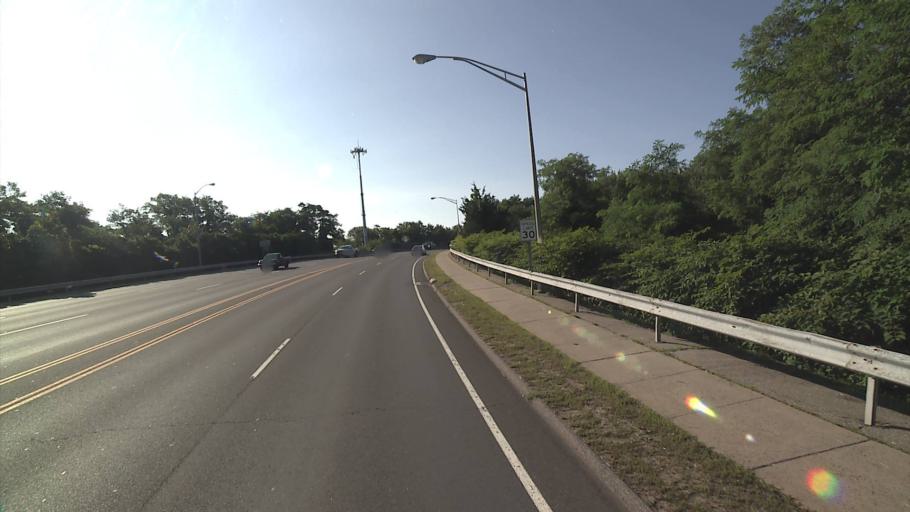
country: US
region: Connecticut
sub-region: Middlesex County
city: Old Saybrook
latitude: 41.3023
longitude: -72.3760
